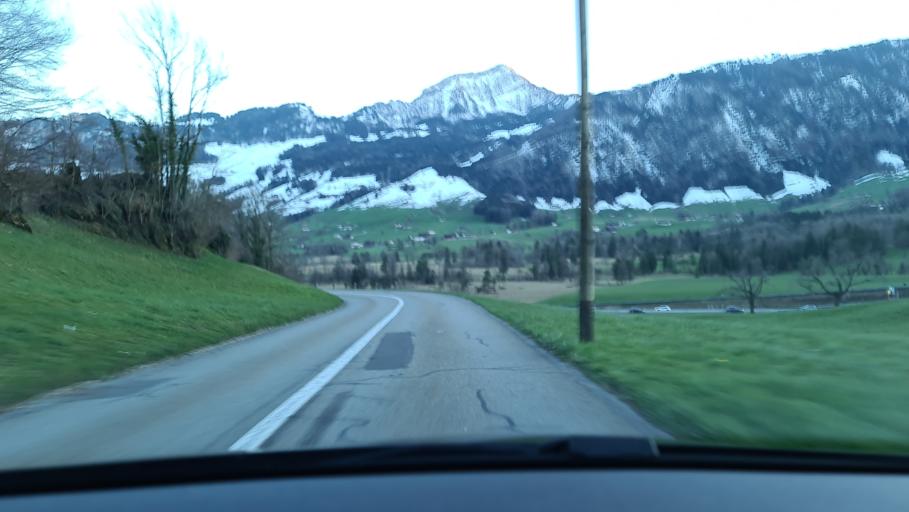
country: CH
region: Schwyz
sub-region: Bezirk Schwyz
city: Goldau
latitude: 47.0513
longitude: 8.5742
